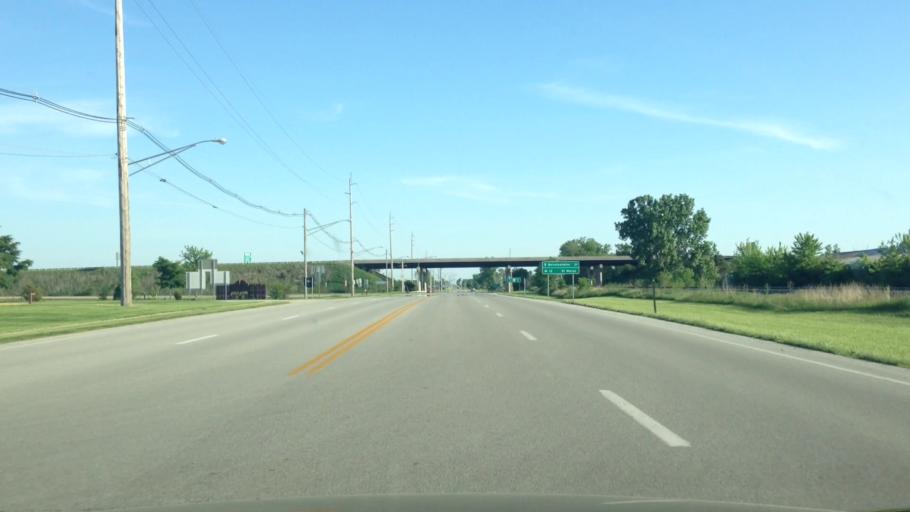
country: US
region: Ohio
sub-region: Auglaize County
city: Wapakoneta
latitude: 40.5583
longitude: -84.1939
